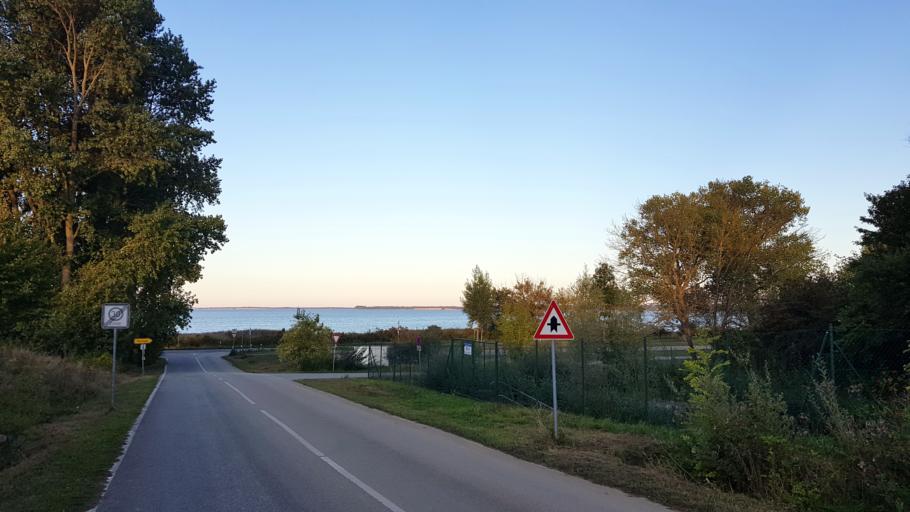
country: DE
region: Mecklenburg-Vorpommern
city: Ostseebad Boltenhagen
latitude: 53.9369
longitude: 11.2489
